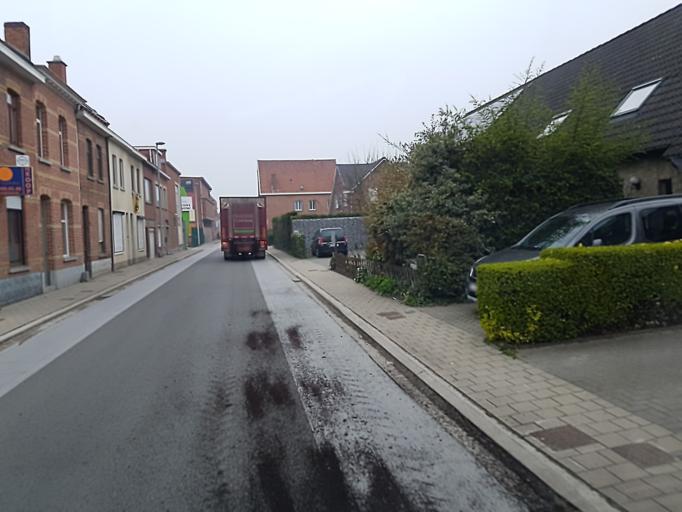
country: BE
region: Flanders
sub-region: Provincie Oost-Vlaanderen
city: Sint-Niklaas
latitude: 51.1751
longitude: 4.1540
